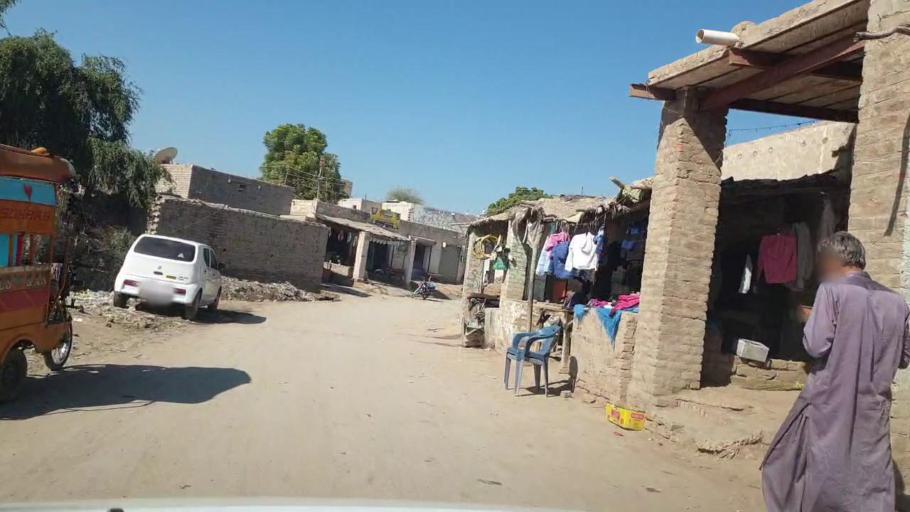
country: PK
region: Sindh
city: Bhan
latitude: 26.6498
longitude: 67.7121
